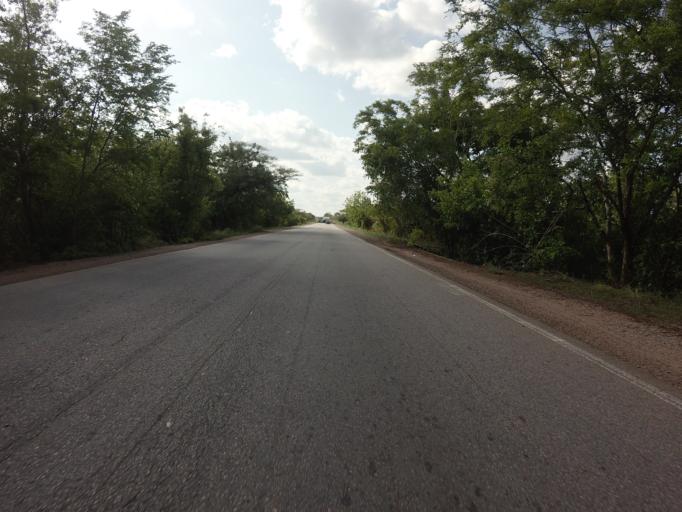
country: GH
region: Upper East
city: Bolgatanga
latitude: 10.5224
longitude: -0.8137
